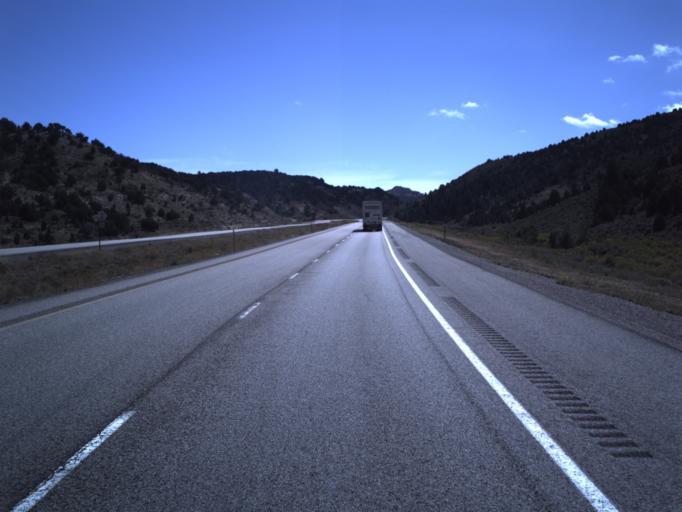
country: US
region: Utah
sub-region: Sevier County
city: Salina
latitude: 38.8008
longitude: -111.5157
